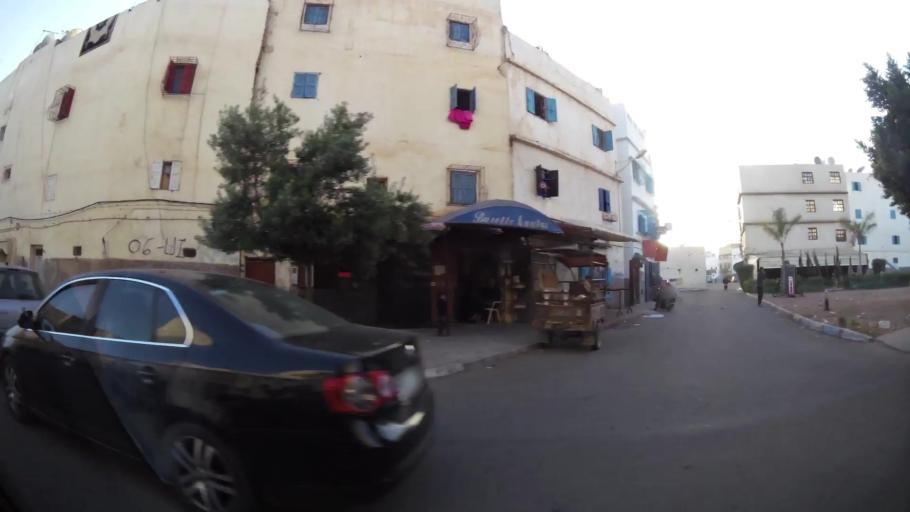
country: MA
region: Oued ed Dahab-Lagouira
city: Dakhla
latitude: 30.3903
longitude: -9.5665
